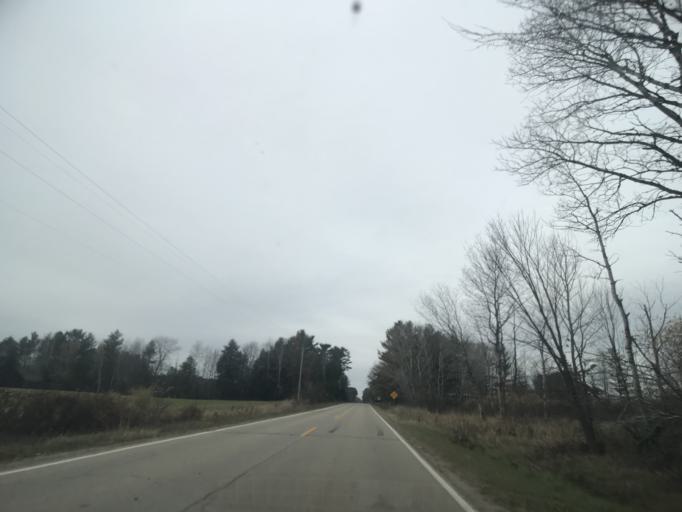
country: US
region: Wisconsin
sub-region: Oconto County
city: Gillett
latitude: 44.9838
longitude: -88.3209
